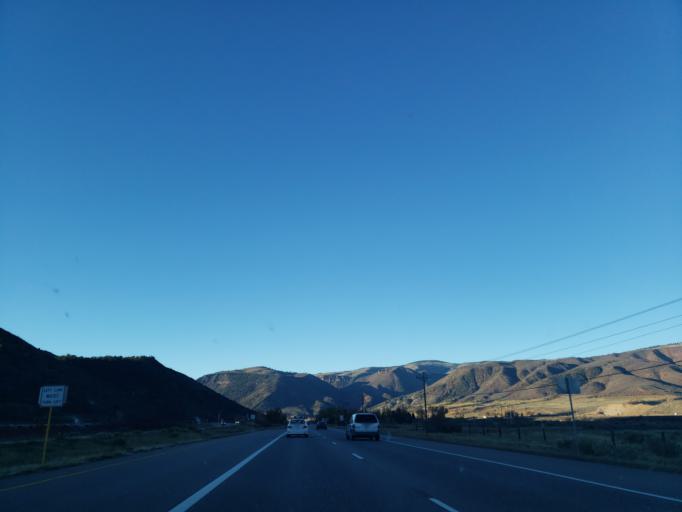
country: US
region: Colorado
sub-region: Pitkin County
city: Snowmass Village
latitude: 39.2569
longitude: -106.8863
